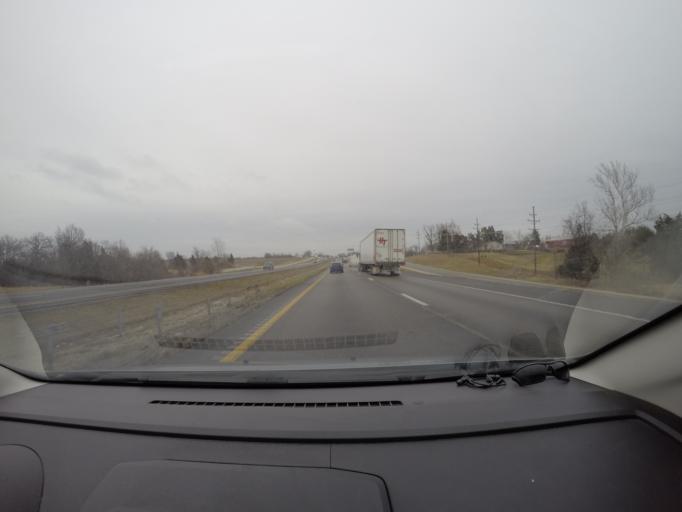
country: US
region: Missouri
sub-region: Warren County
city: Warrenton
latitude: 38.8499
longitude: -91.2860
